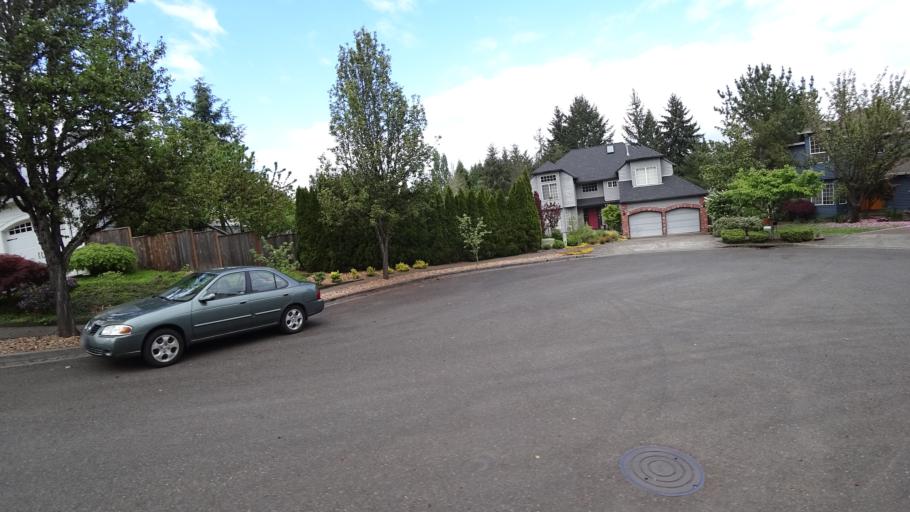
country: US
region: Oregon
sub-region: Washington County
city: Beaverton
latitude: 45.4481
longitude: -122.8388
